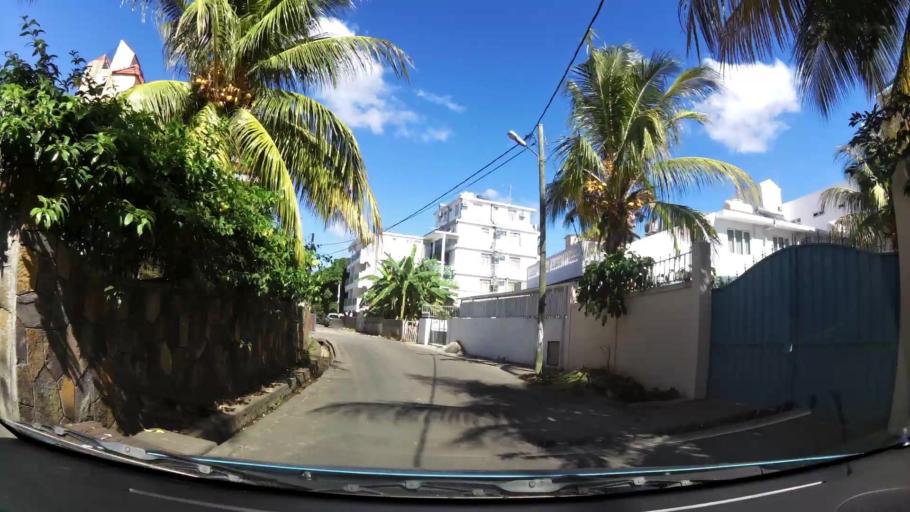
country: MU
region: Black River
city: Flic en Flac
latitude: -20.2780
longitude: 57.3694
